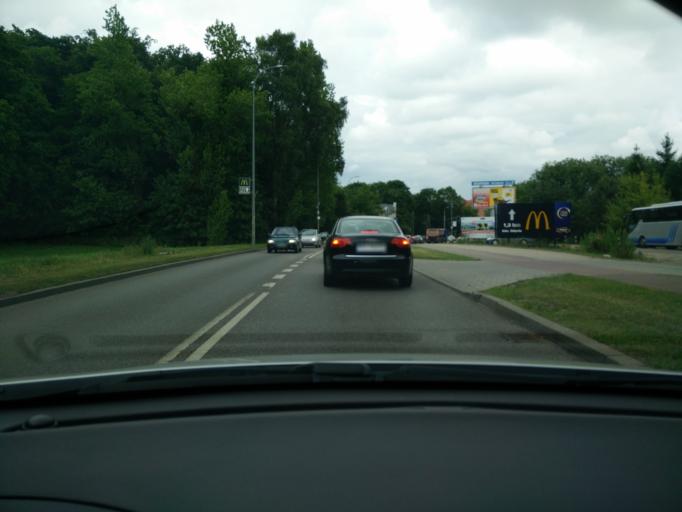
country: PL
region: Pomeranian Voivodeship
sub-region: Sopot
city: Sopot
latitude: 54.4105
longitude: 18.5515
